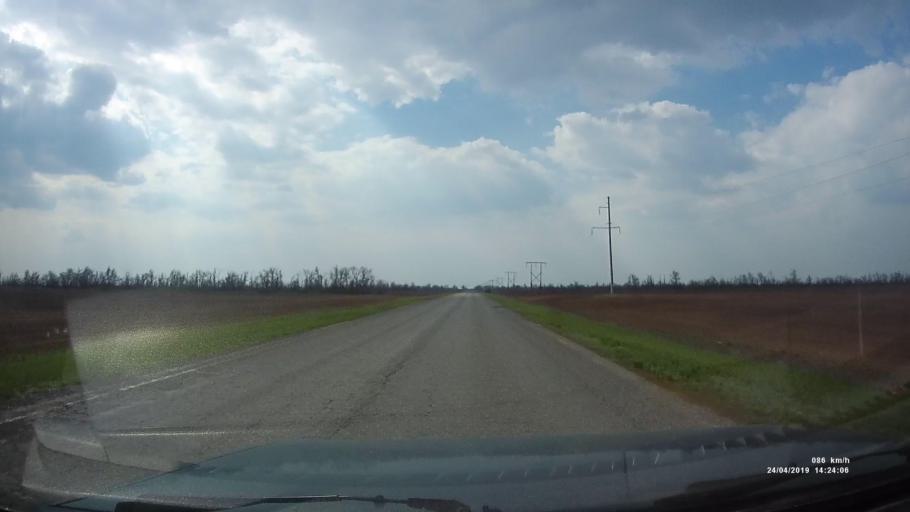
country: RU
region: Kalmykiya
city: Arshan'
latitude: 46.3267
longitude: 44.1040
